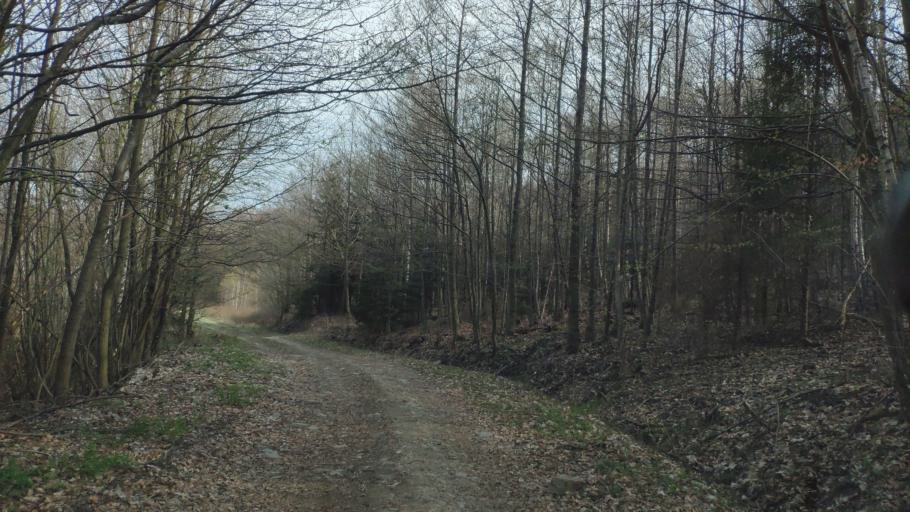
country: SK
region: Kosicky
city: Moldava nad Bodvou
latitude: 48.7357
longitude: 21.0575
